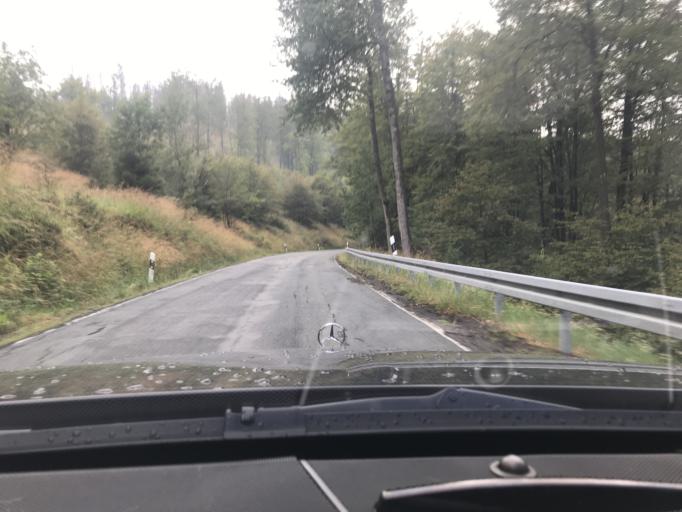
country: DE
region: Lower Saxony
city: Sankt Andreasberg
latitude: 51.6986
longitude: 10.5562
